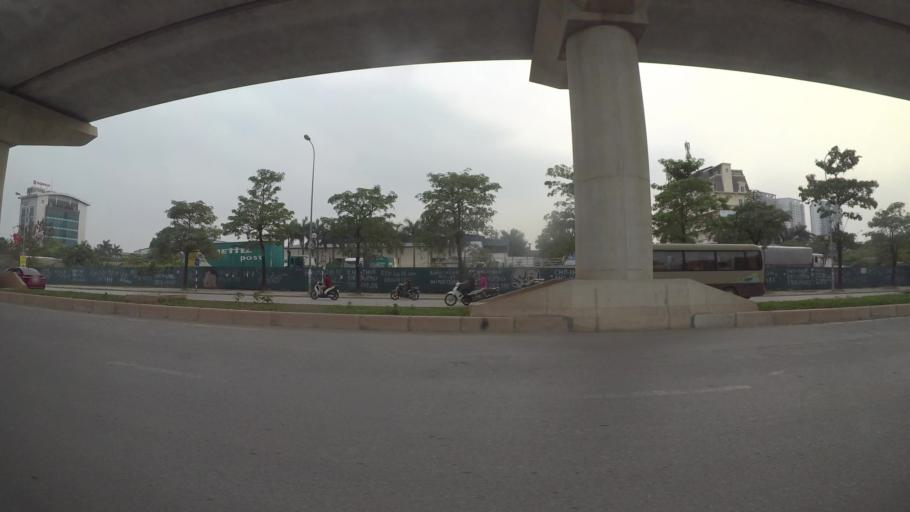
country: VN
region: Ha Noi
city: Cau Dien
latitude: 21.0502
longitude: 105.7394
